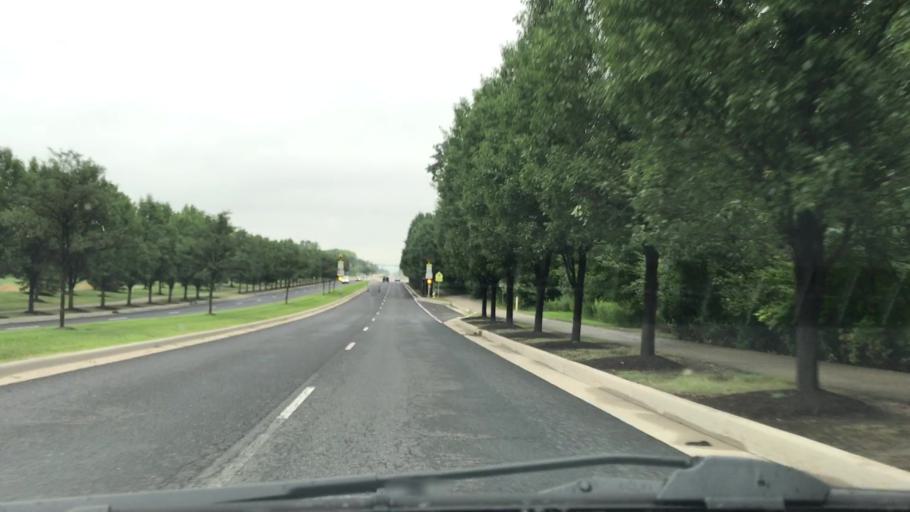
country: US
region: Indiana
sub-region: Hamilton County
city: Carmel
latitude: 40.0081
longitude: -86.0705
